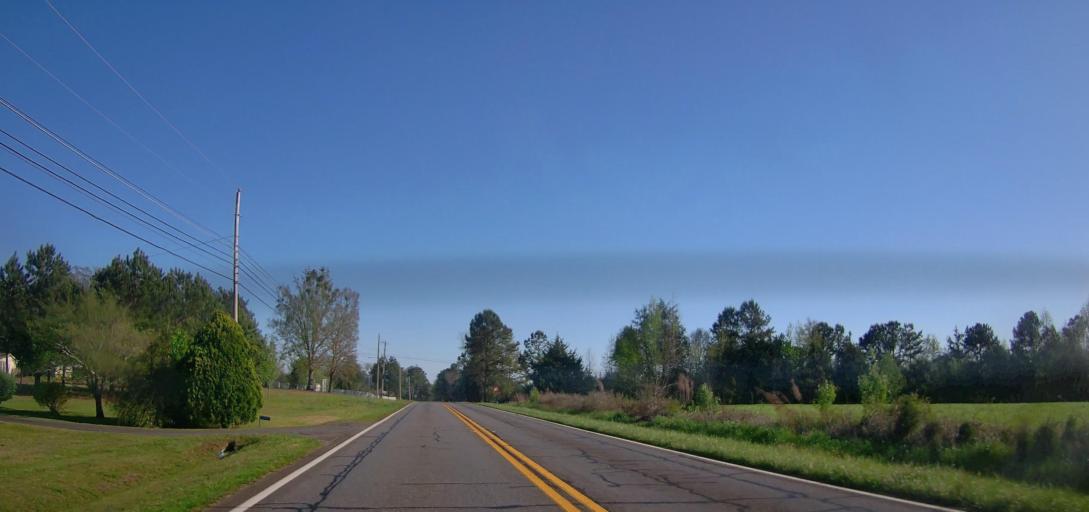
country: US
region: Georgia
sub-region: Monroe County
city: Forsyth
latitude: 33.0714
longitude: -83.9558
